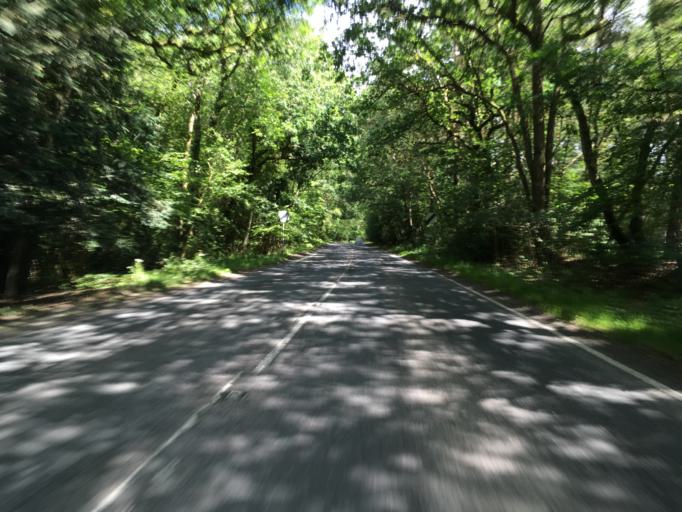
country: GB
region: England
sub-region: Hampshire
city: Highclere
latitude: 51.3564
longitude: -1.3670
